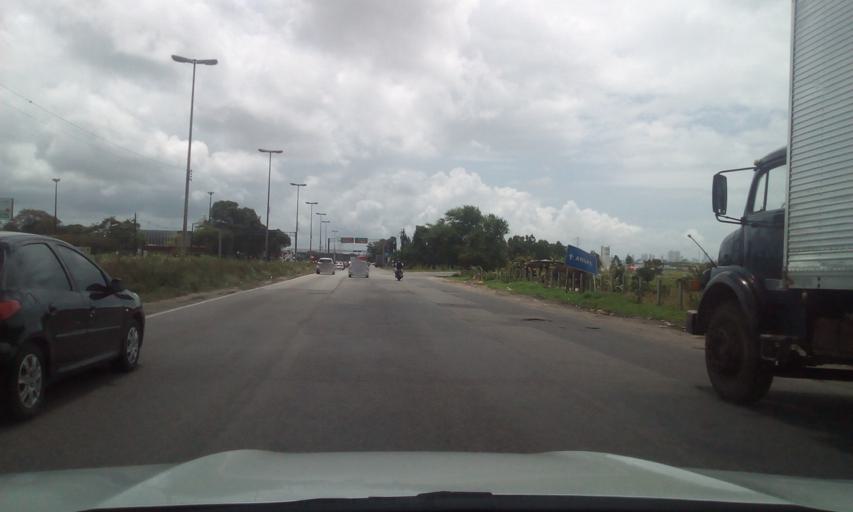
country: BR
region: Pernambuco
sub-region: Recife
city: Recife
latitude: -8.0750
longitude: -34.9427
